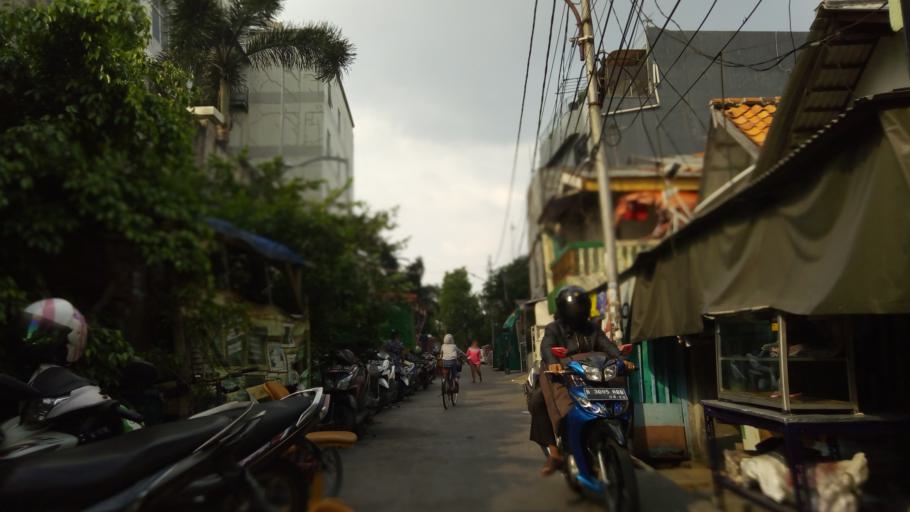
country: ID
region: Jakarta Raya
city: Jakarta
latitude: -6.1502
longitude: 106.8337
